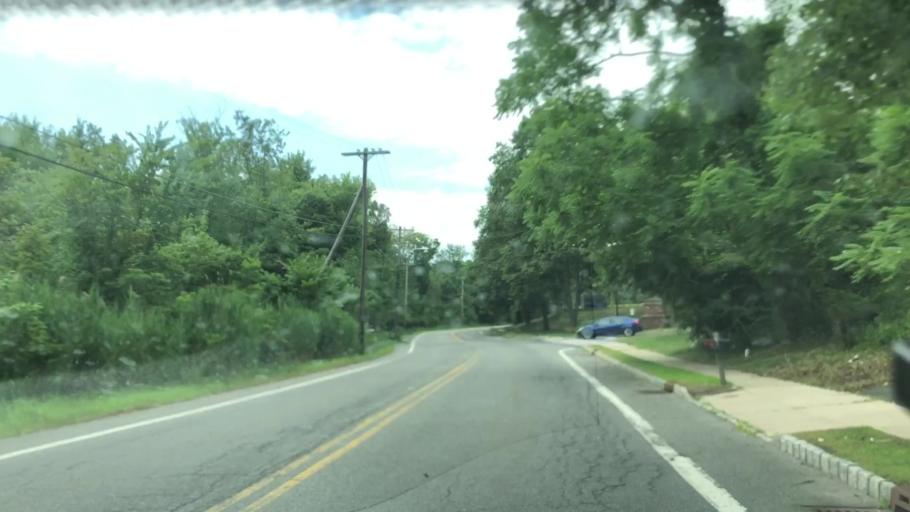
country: US
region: New Jersey
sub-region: Morris County
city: Mount Arlington
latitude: 40.9187
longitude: -74.6364
